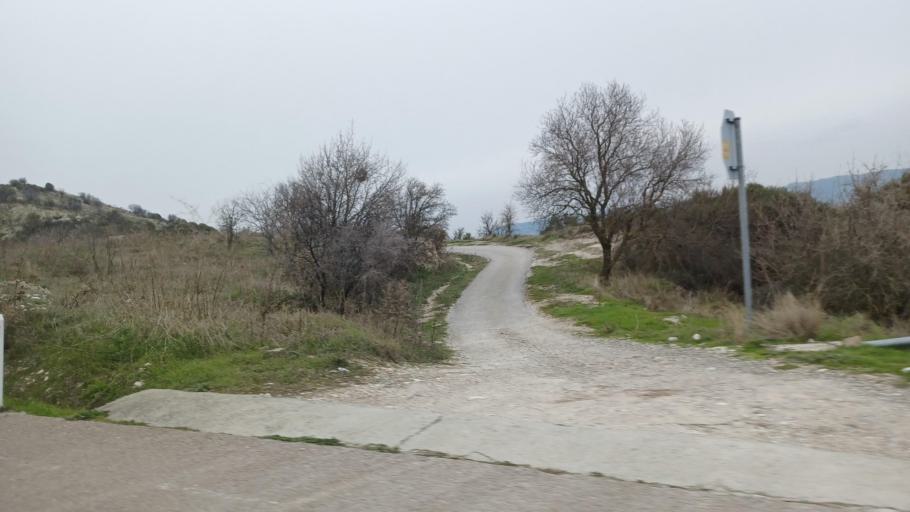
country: CY
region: Limassol
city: Pachna
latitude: 34.8255
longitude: 32.6849
